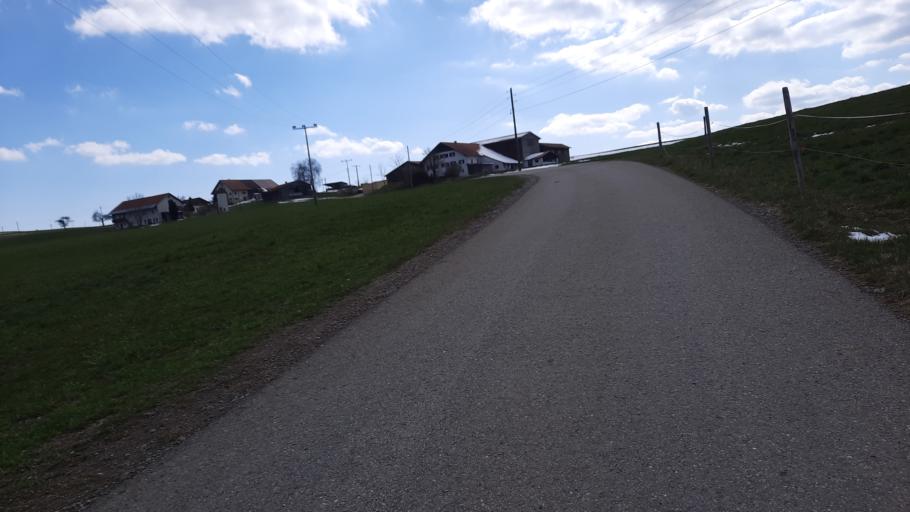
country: DE
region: Bavaria
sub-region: Swabia
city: Altusried
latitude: 47.8197
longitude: 10.2136
